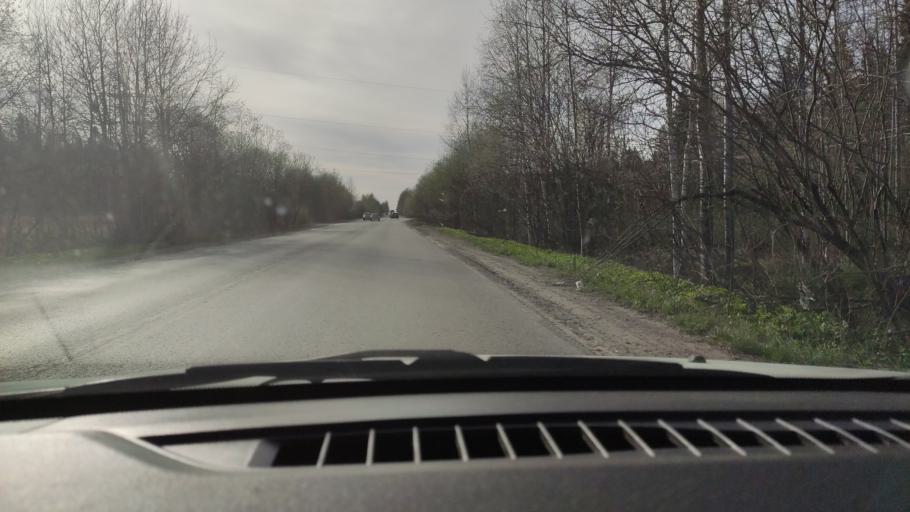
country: RU
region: Perm
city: Ferma
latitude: 57.9395
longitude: 56.4499
